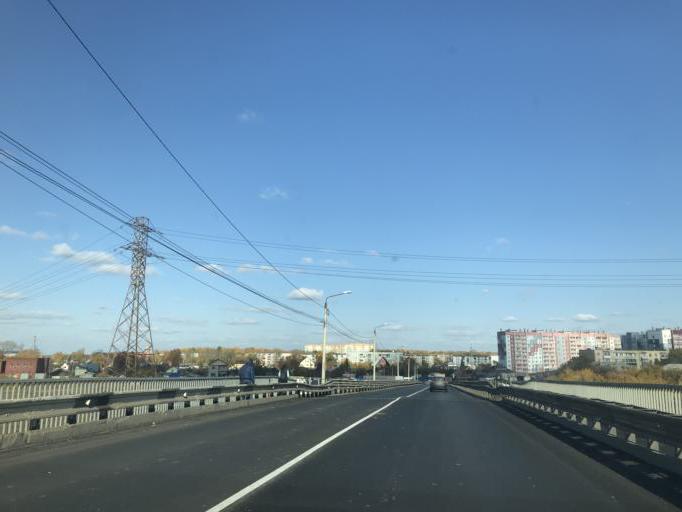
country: RU
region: Chelyabinsk
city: Roshchino
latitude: 55.2338
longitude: 61.2937
